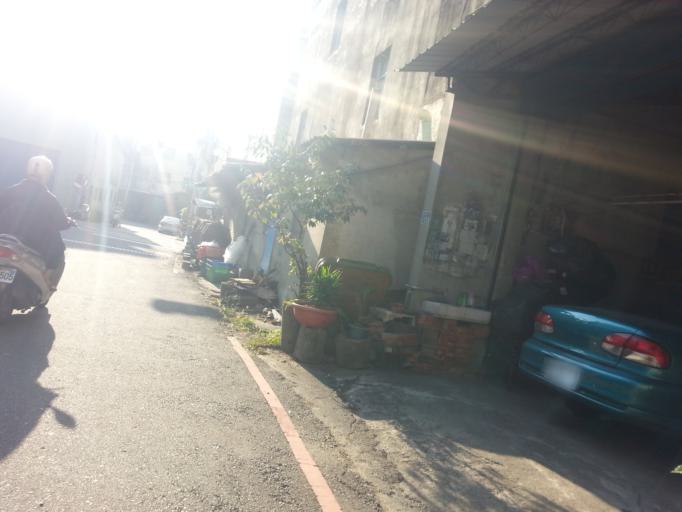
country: TW
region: Taiwan
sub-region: Changhua
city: Chang-hua
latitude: 24.0905
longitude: 120.5485
